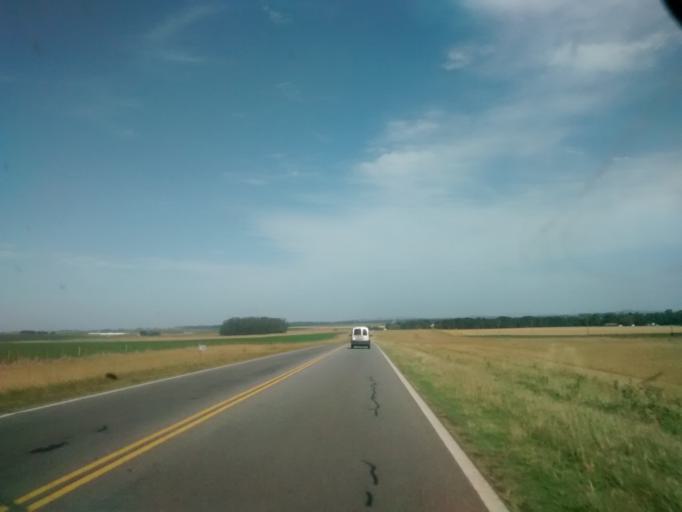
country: AR
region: Buenos Aires
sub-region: Partido de Balcarce
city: Balcarce
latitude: -37.6462
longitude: -58.5853
